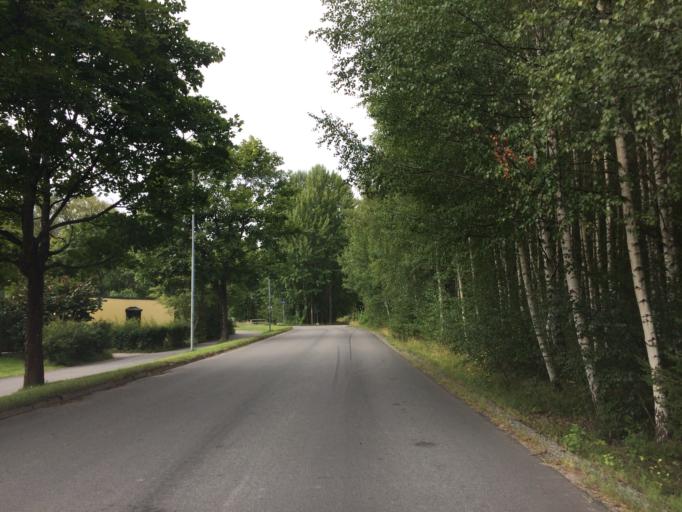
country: SE
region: Stockholm
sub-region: Upplands Vasby Kommun
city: Upplands Vaesby
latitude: 59.4651
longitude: 17.9094
